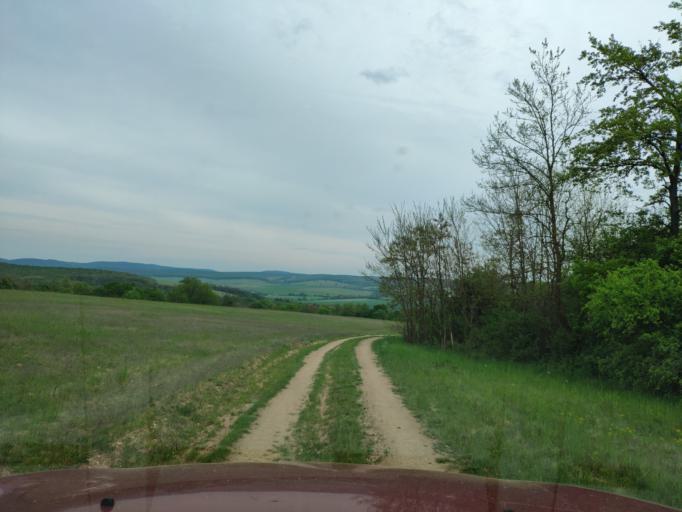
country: HU
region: Borsod-Abauj-Zemplen
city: Putnok
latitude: 48.4911
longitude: 20.3266
